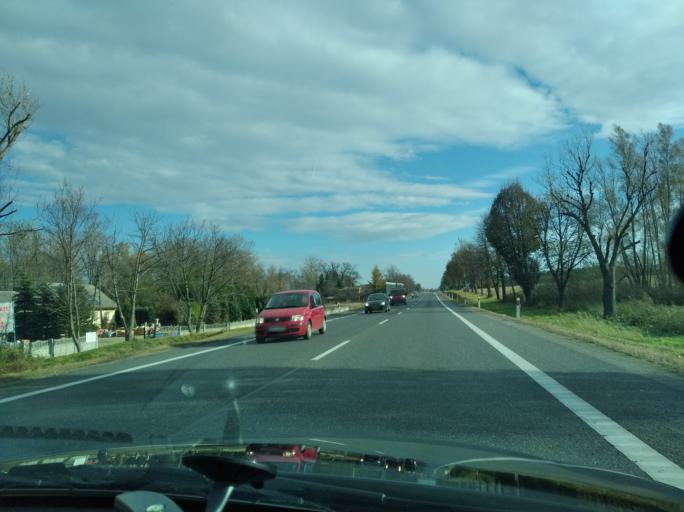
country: PL
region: Subcarpathian Voivodeship
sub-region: Powiat debicki
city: Brzeznica
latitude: 50.0610
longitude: 21.4944
